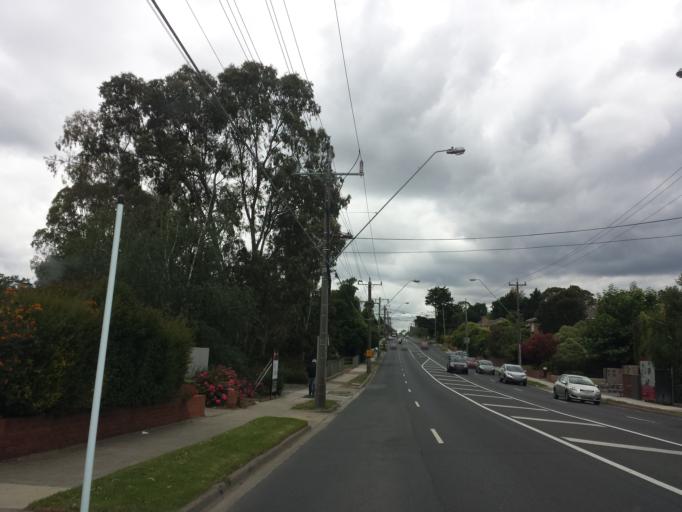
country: AU
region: Victoria
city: Rosanna
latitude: -37.7539
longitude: 145.0700
